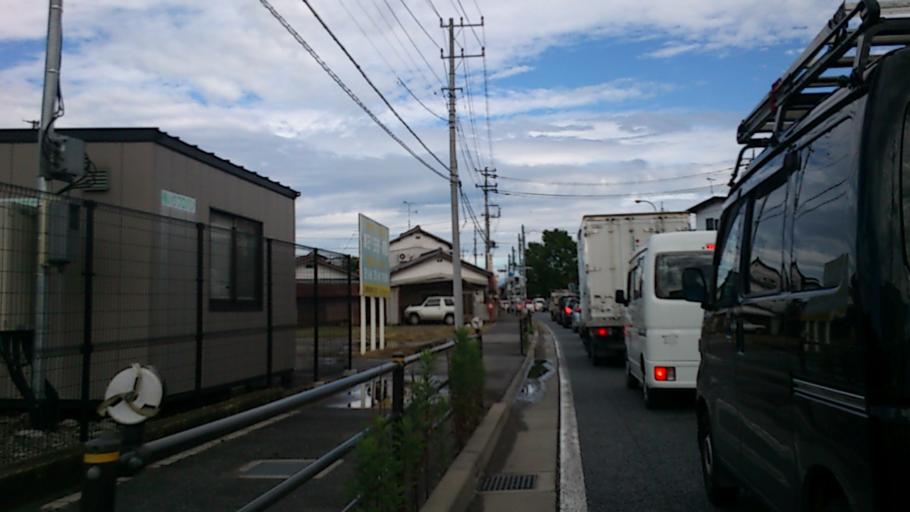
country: JP
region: Gunma
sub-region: Sawa-gun
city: Tamamura
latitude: 36.2655
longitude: 139.1274
